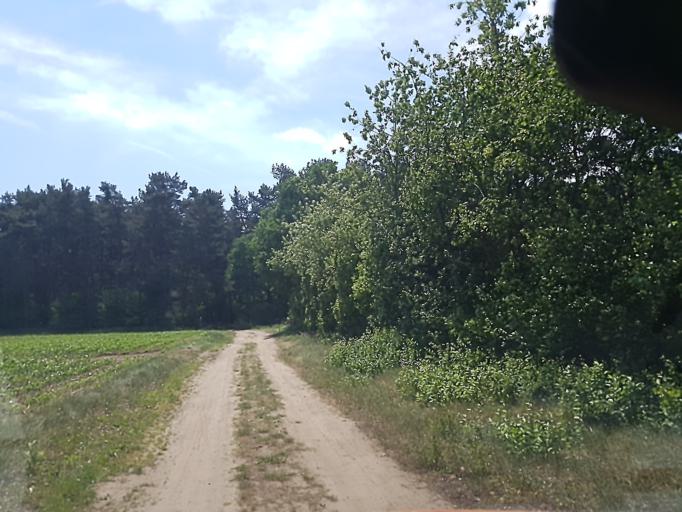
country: DE
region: Brandenburg
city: Gorzke
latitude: 52.1259
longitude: 12.3125
